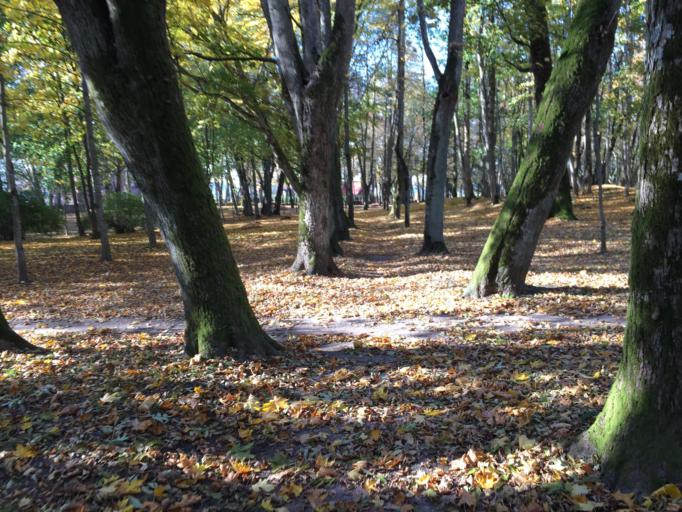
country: LT
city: Salantai
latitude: 55.9992
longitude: 21.6806
